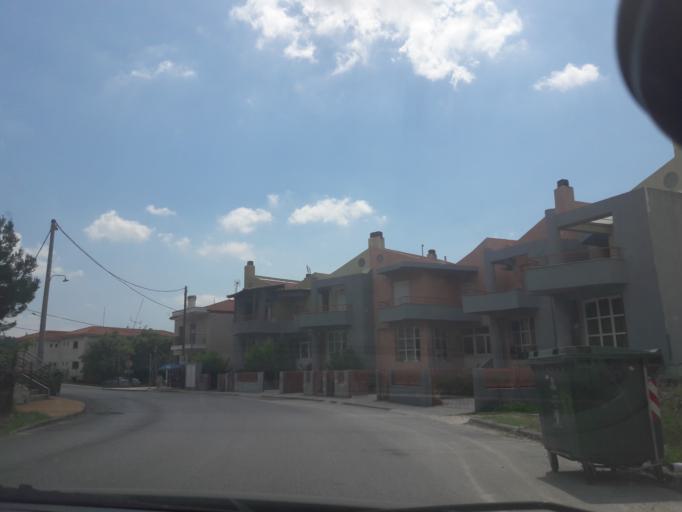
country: GR
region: Central Macedonia
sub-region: Nomos Chalkidikis
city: Polygyros
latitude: 40.3768
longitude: 23.4500
